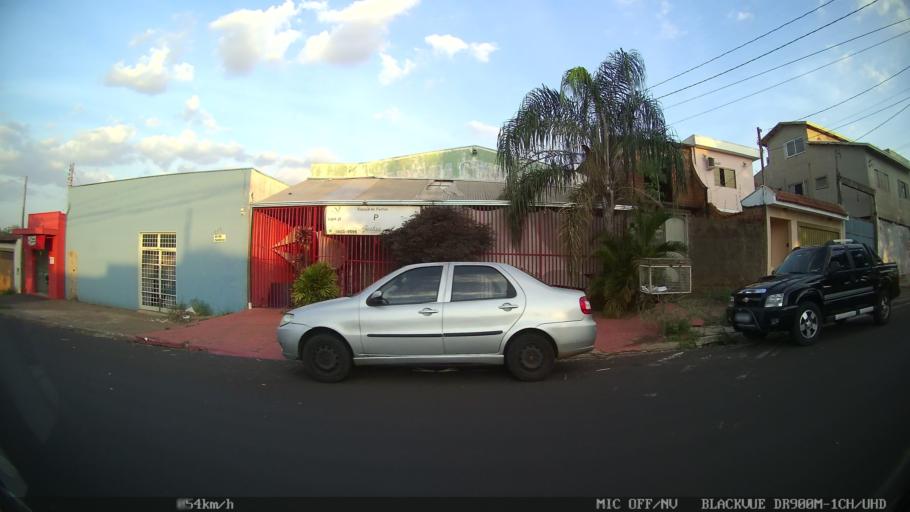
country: BR
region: Sao Paulo
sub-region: Ribeirao Preto
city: Ribeirao Preto
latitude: -21.1342
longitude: -47.8442
